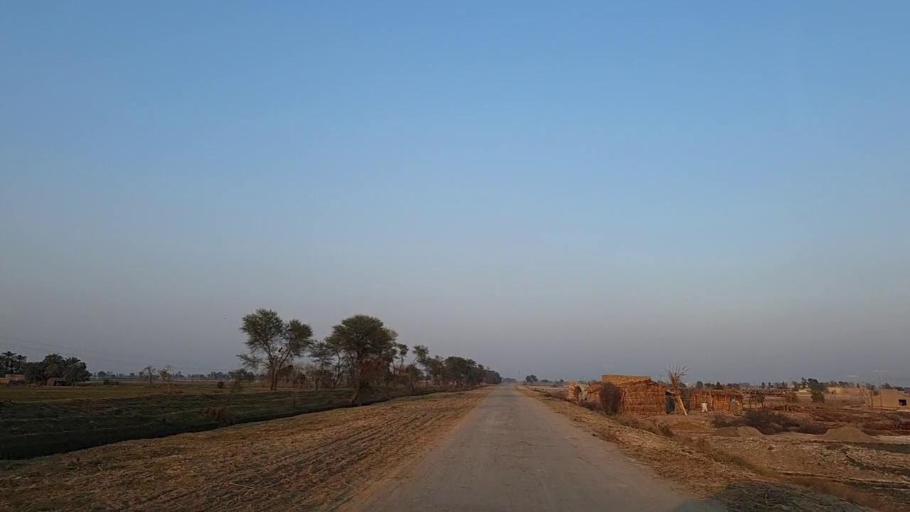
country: PK
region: Sindh
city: Naushahro Firoz
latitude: 26.7731
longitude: 68.0601
